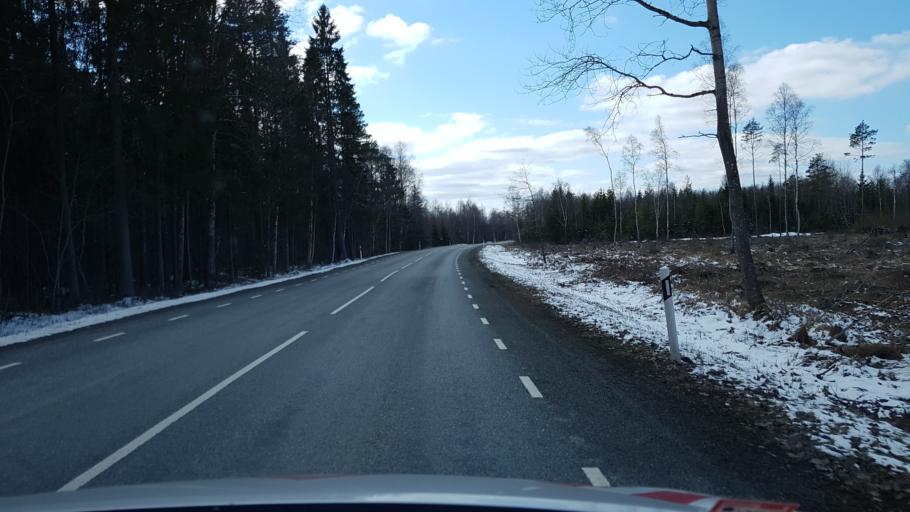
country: EE
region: Laeaene-Virumaa
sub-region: Tapa vald
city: Tapa
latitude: 59.2765
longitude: 25.9885
